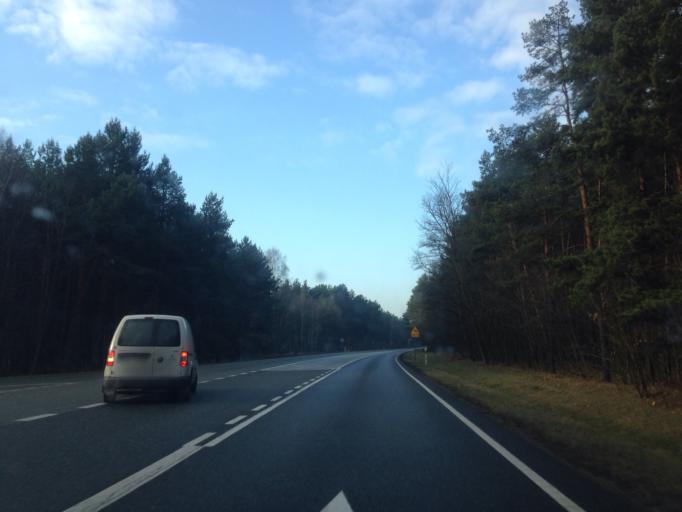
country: PL
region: Kujawsko-Pomorskie
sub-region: Powiat torunski
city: Wielka Nieszawka
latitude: 52.9841
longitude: 18.4869
